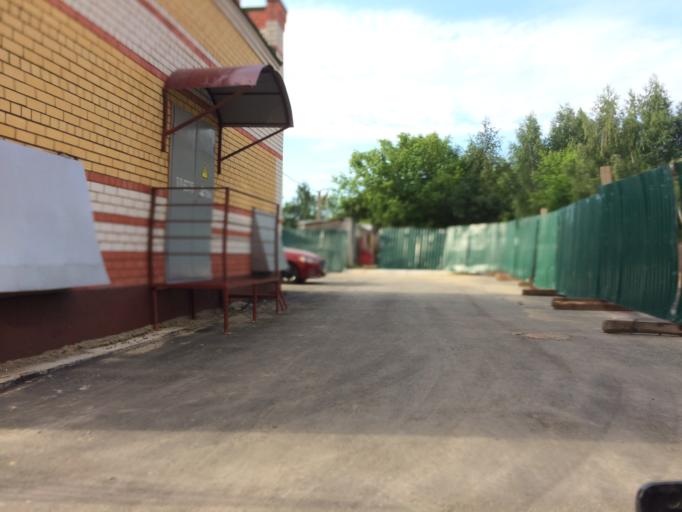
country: RU
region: Mariy-El
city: Yoshkar-Ola
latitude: 56.6423
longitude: 47.8533
